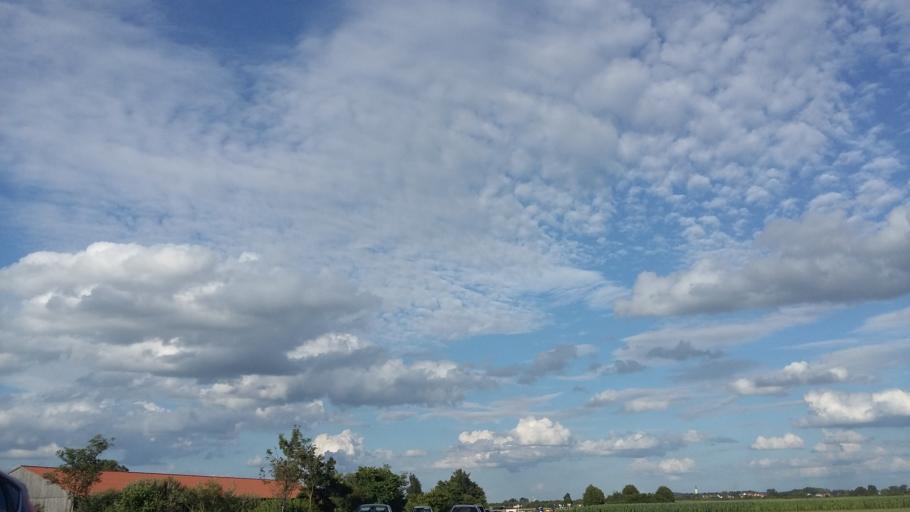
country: DE
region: Bavaria
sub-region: Swabia
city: Mering
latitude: 48.2679
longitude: 10.9509
